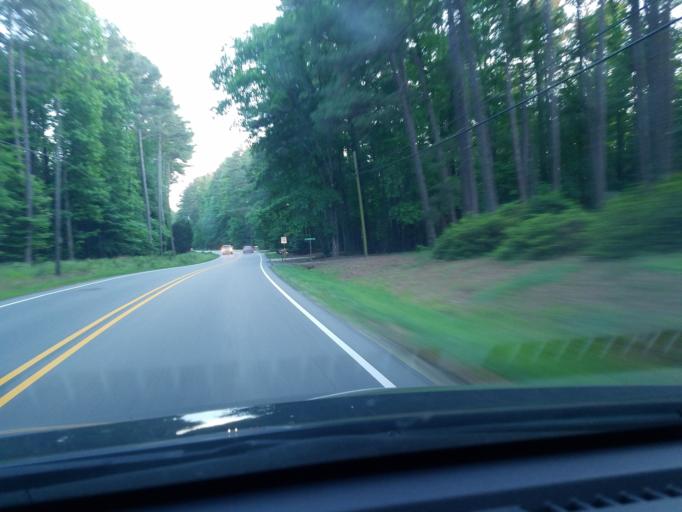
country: US
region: North Carolina
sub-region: Durham County
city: Durham
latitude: 35.9408
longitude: -78.9441
